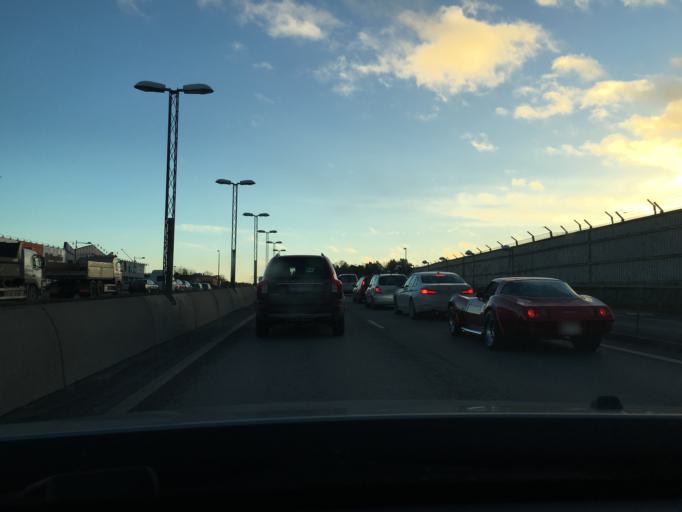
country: SE
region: Stockholm
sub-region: Sundbybergs Kommun
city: Sundbyberg
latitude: 59.3496
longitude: 17.9566
